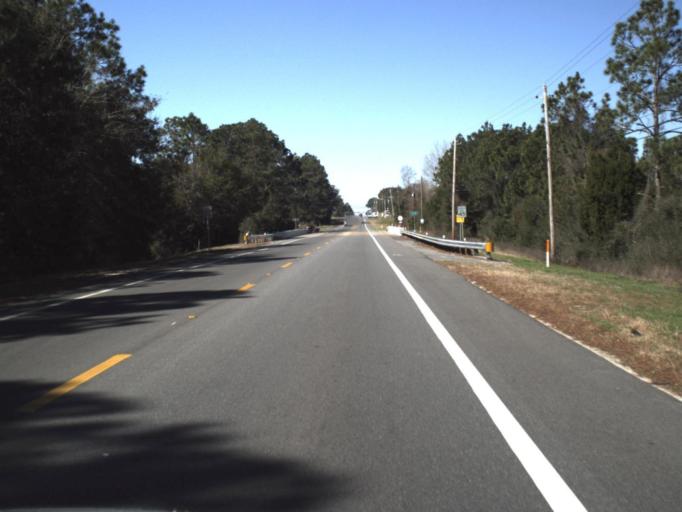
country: US
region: Florida
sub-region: Bay County
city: Callaway
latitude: 30.1529
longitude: -85.5562
